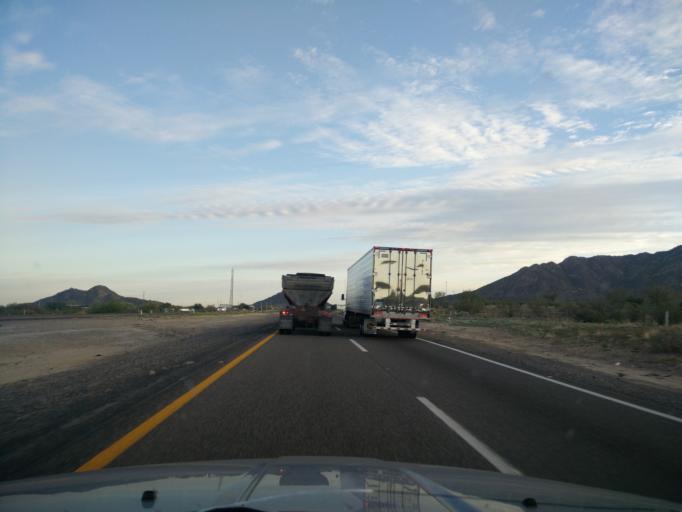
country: MX
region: Sonora
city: Hermosillo
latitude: 28.9545
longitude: -110.9626
